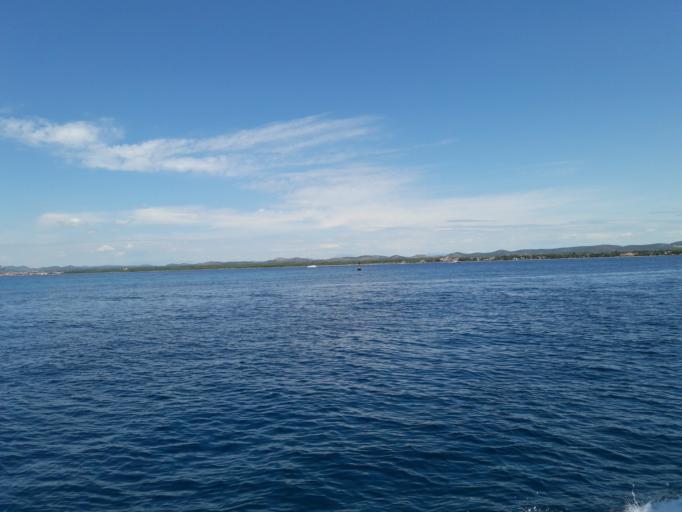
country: HR
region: Sibensko-Kniniska
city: Vodice
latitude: 43.7096
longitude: 15.8324
